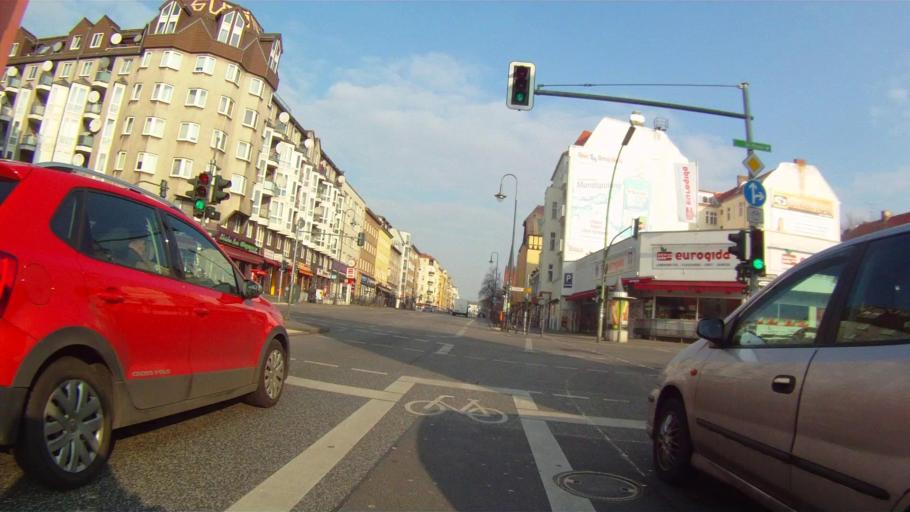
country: DE
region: Berlin
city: Berlin Treptow
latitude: 52.4695
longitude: 13.4418
